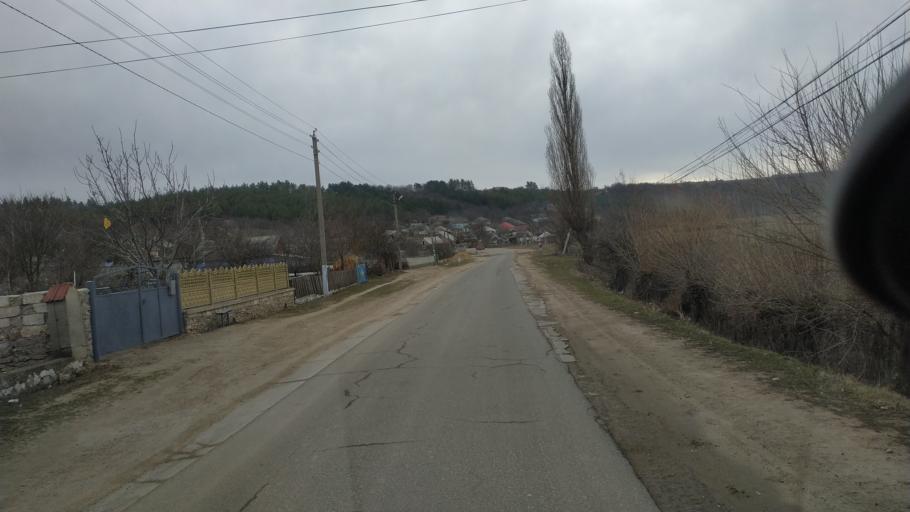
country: MD
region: Telenesti
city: Cocieri
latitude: 47.2677
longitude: 29.0699
